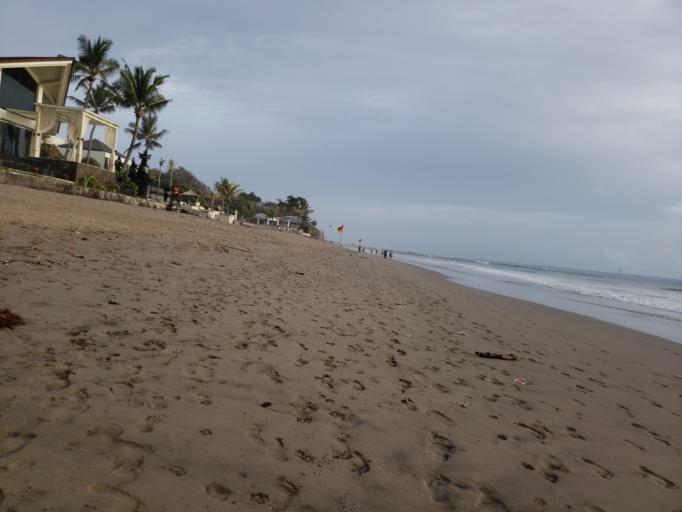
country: ID
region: Bali
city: Kuta
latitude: -8.6857
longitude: 115.1532
